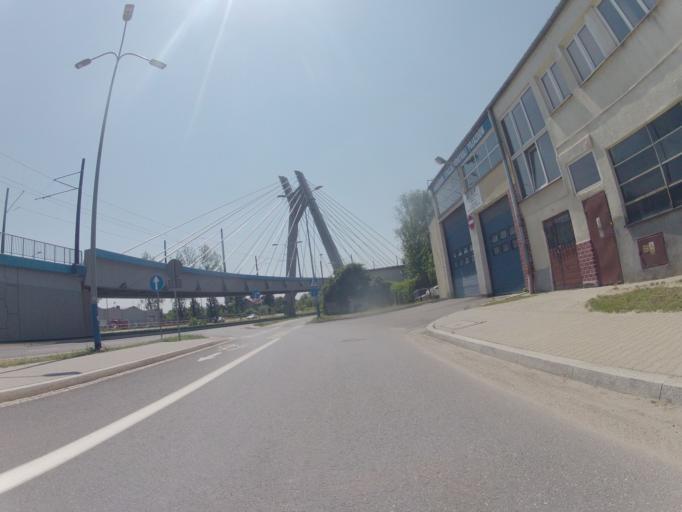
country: PL
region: Lesser Poland Voivodeship
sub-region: Krakow
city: Krakow
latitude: 50.0381
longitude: 19.9826
